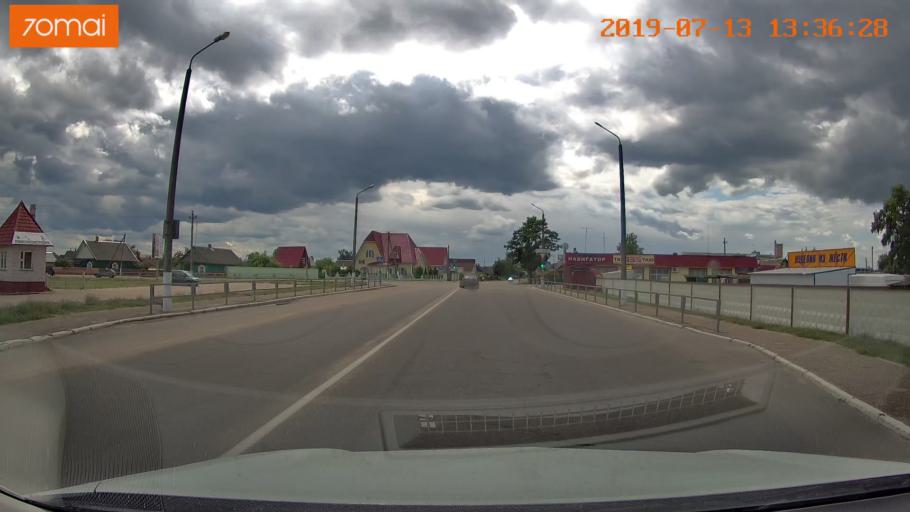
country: BY
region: Mogilev
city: Asipovichy
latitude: 53.3019
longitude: 28.6229
